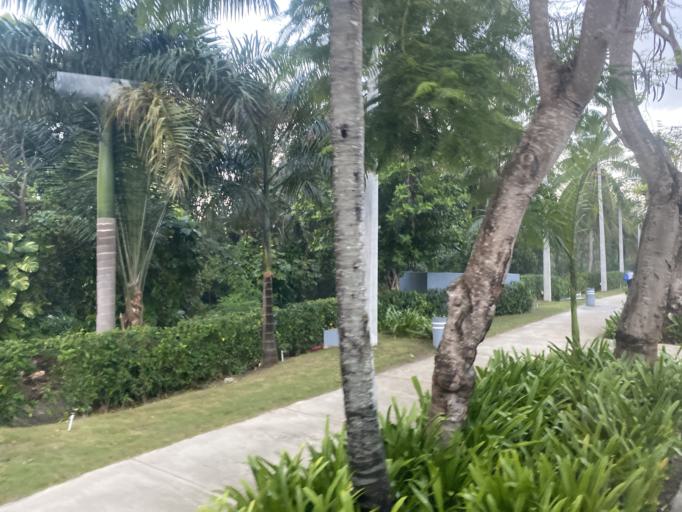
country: DO
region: San Juan
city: Punta Cana
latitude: 18.7192
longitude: -68.4568
